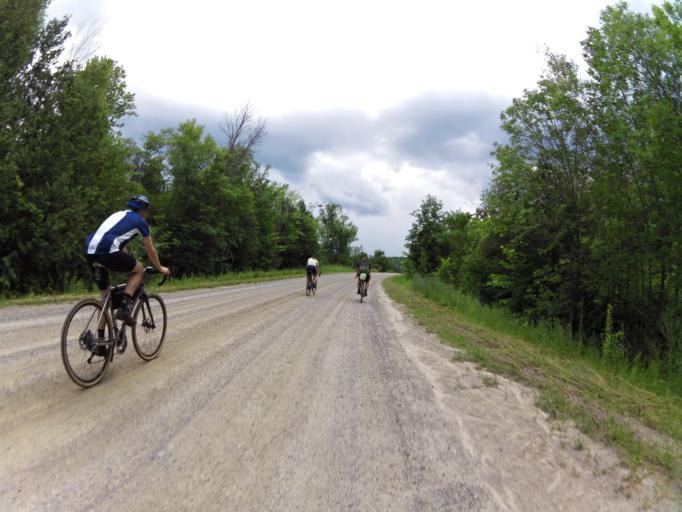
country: CA
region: Ontario
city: Renfrew
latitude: 45.1336
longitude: -76.6301
